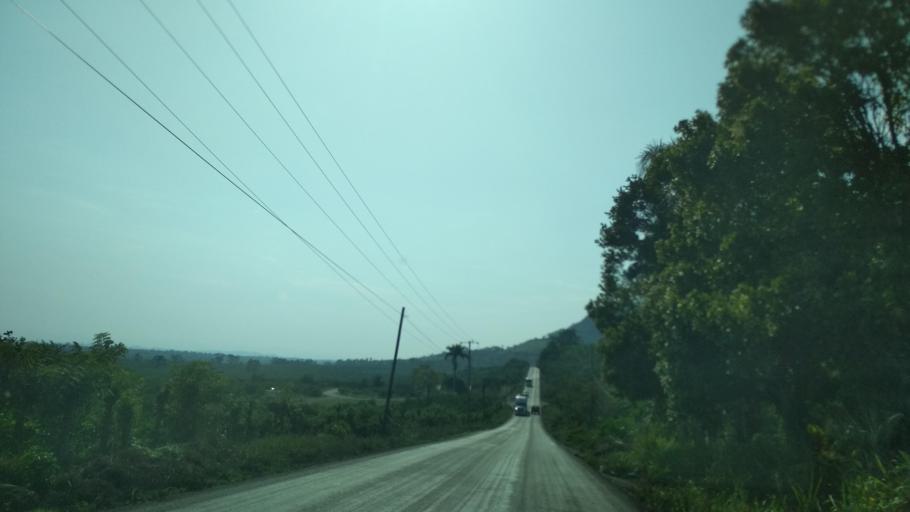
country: MX
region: Veracruz
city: Agua Dulce
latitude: 20.3965
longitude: -97.2688
